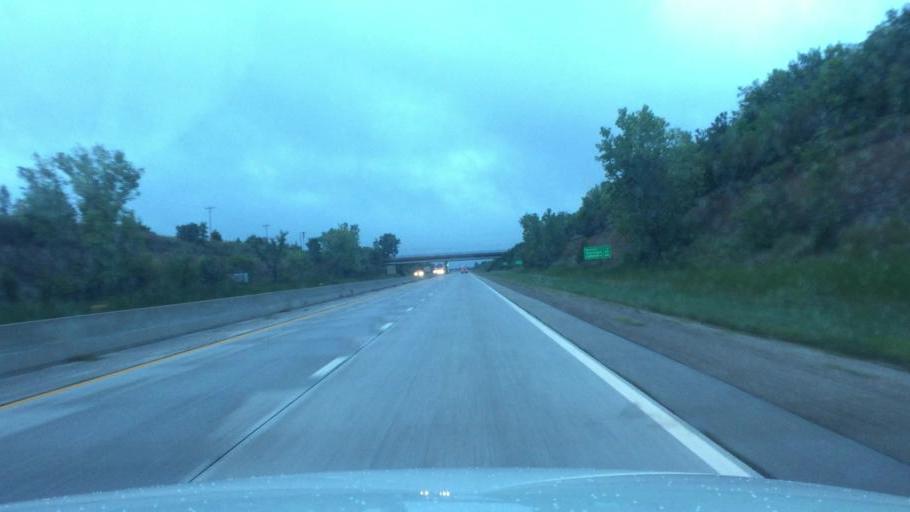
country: US
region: Kansas
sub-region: Neosho County
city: Chanute
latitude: 37.6782
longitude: -95.4796
